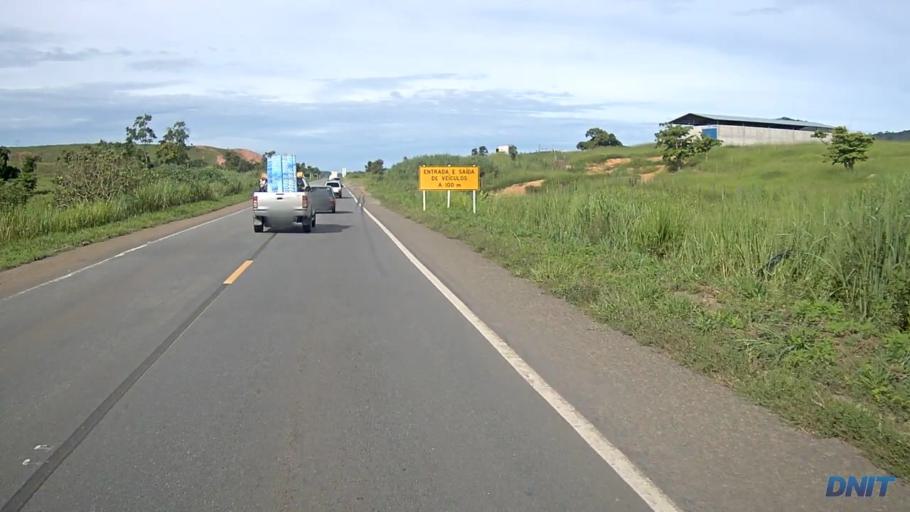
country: BR
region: Minas Gerais
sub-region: Belo Oriente
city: Belo Oriente
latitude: -19.1915
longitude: -42.2745
